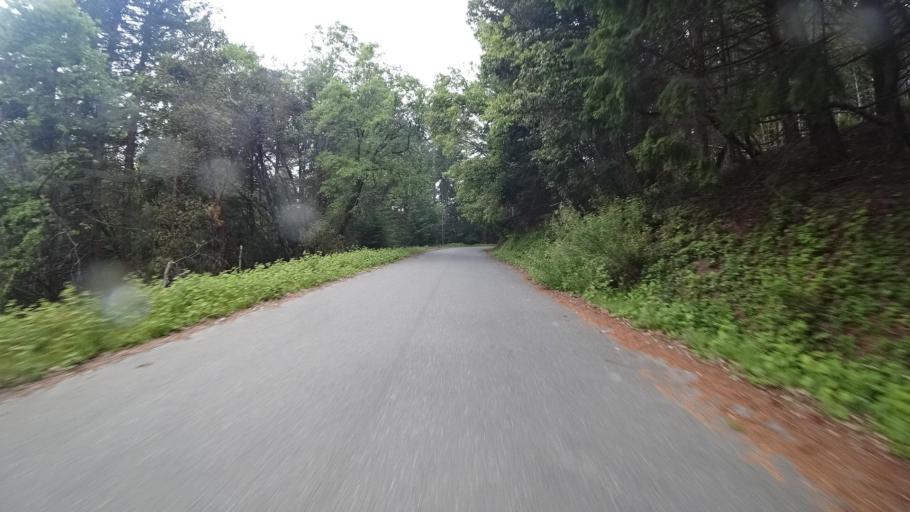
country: US
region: California
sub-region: Humboldt County
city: Willow Creek
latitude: 41.1180
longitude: -123.7341
